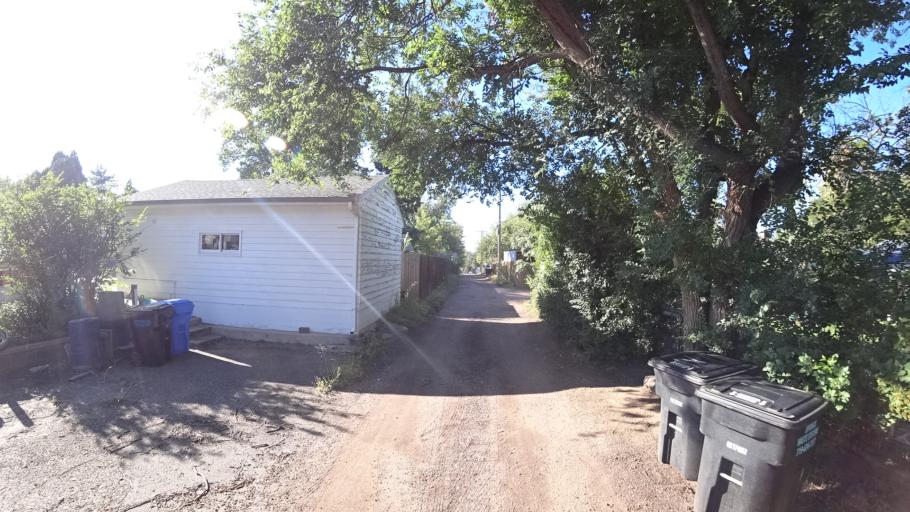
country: US
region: Colorado
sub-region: El Paso County
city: Colorado Springs
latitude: 38.8688
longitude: -104.7958
